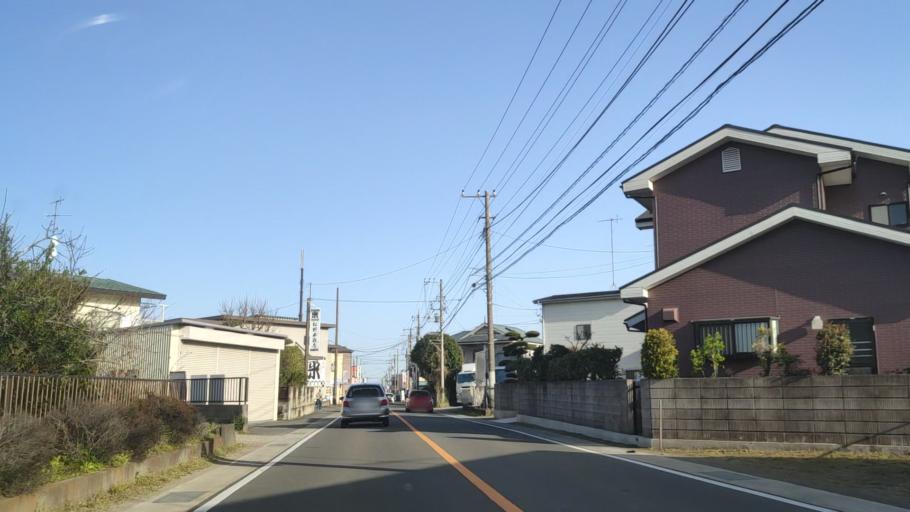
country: JP
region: Kanagawa
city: Zama
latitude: 35.5034
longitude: 139.3527
